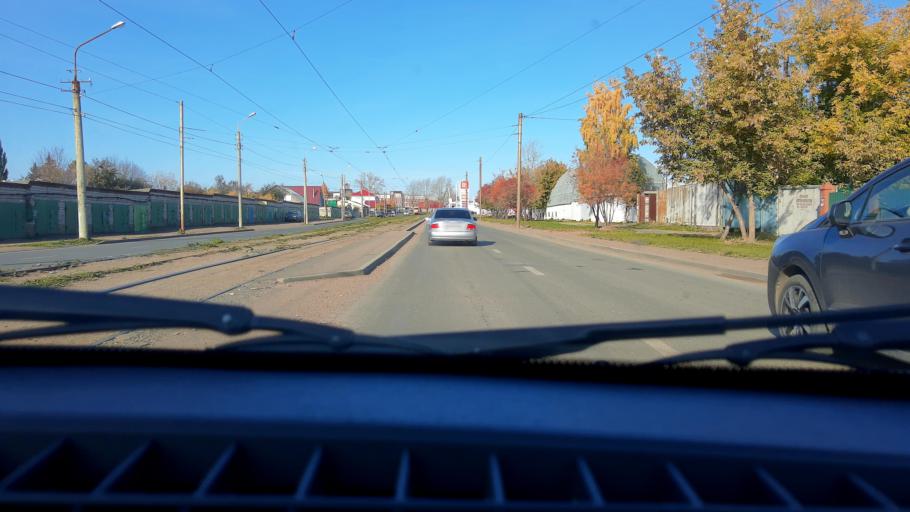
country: RU
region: Bashkortostan
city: Ufa
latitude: 54.8240
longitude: 56.0990
